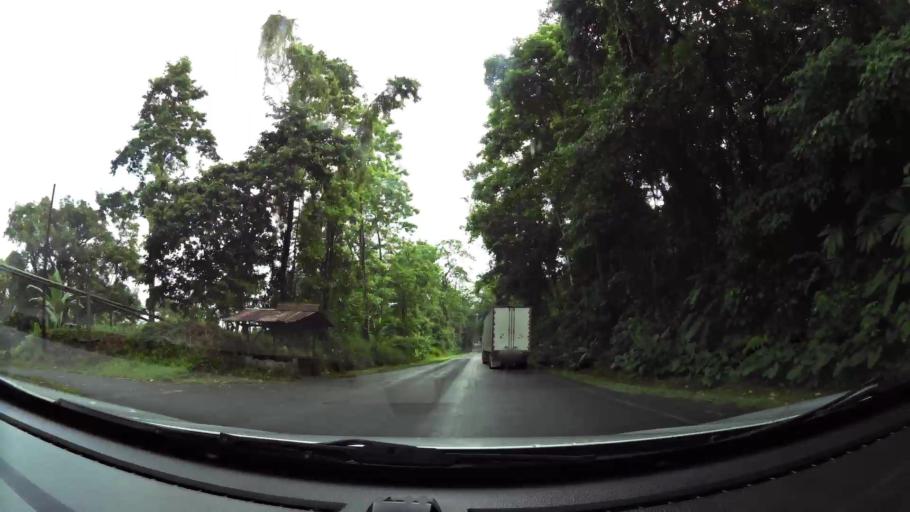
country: CR
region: Limon
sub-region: Canton de Siquirres
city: Pacuarito
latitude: 10.1014
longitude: -83.4658
